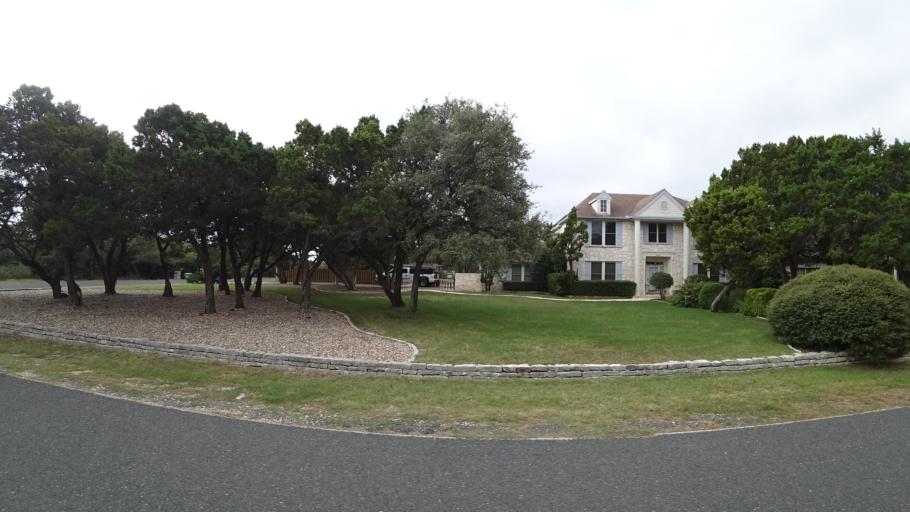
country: US
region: Texas
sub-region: Travis County
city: Barton Creek
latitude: 30.2502
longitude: -97.9112
